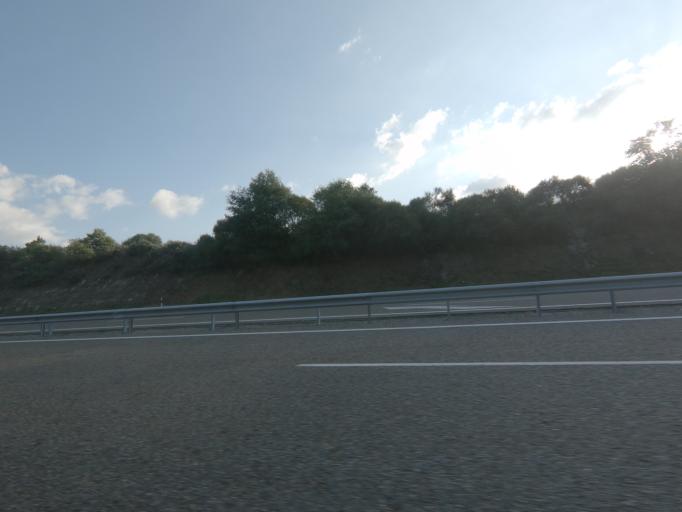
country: ES
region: Galicia
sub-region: Provincia de Ourense
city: Cualedro
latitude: 41.9959
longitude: -7.5601
